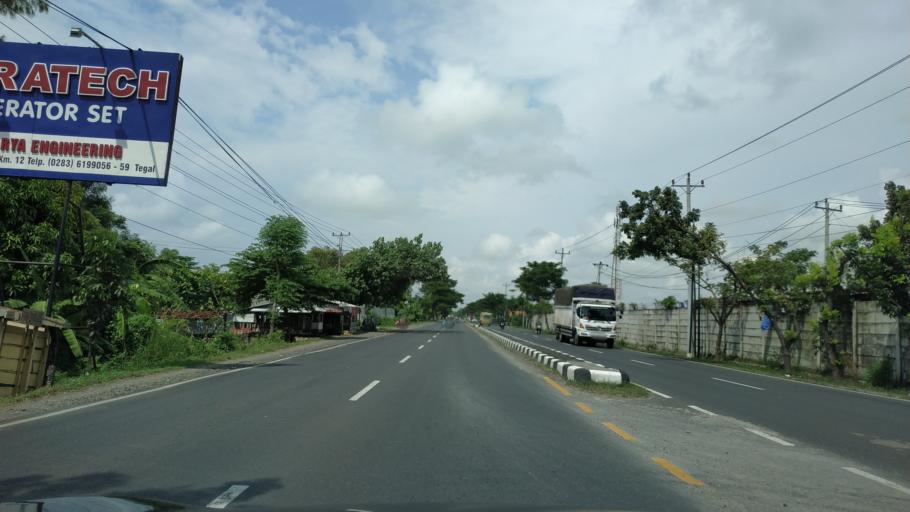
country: ID
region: Central Java
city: Tarub
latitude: -6.8725
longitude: 109.2465
